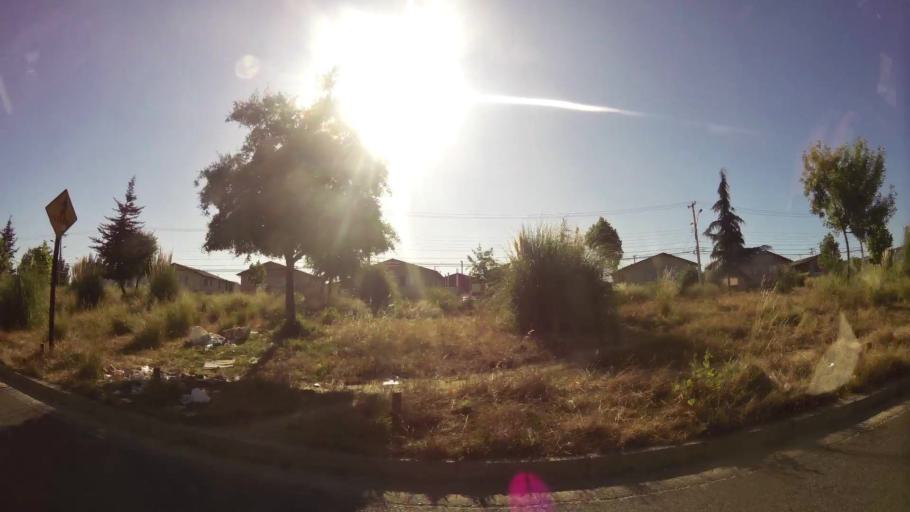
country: CL
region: Valparaiso
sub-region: Provincia de Valparaiso
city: Valparaiso
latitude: -33.1192
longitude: -71.5795
